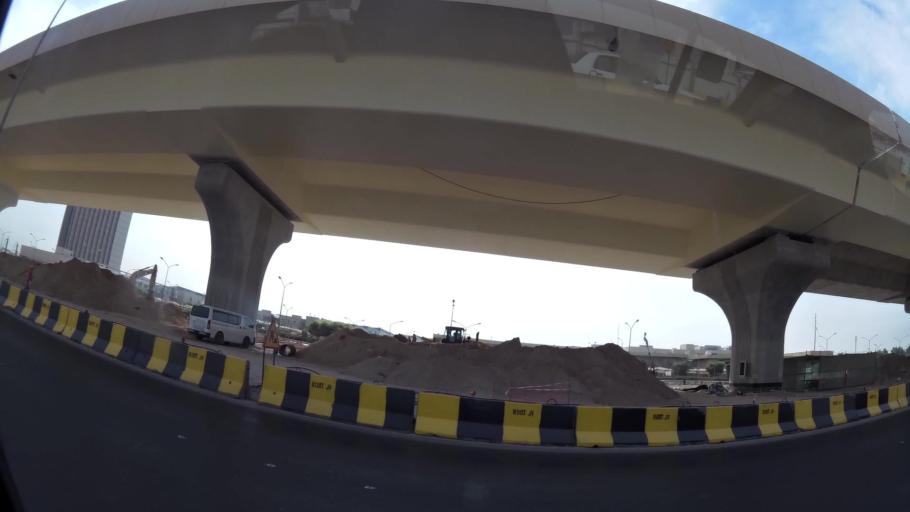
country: KW
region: Al Asimah
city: Ar Rabiyah
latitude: 29.3340
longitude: 47.9122
